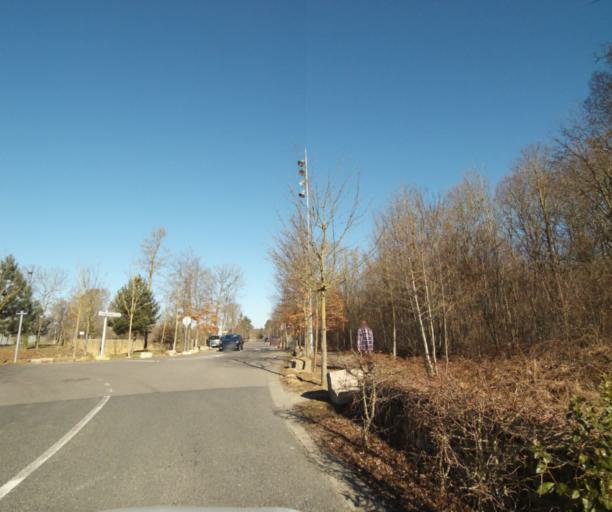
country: FR
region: Lorraine
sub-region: Departement de Meurthe-et-Moselle
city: Maxeville
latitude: 48.7063
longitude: 6.1551
